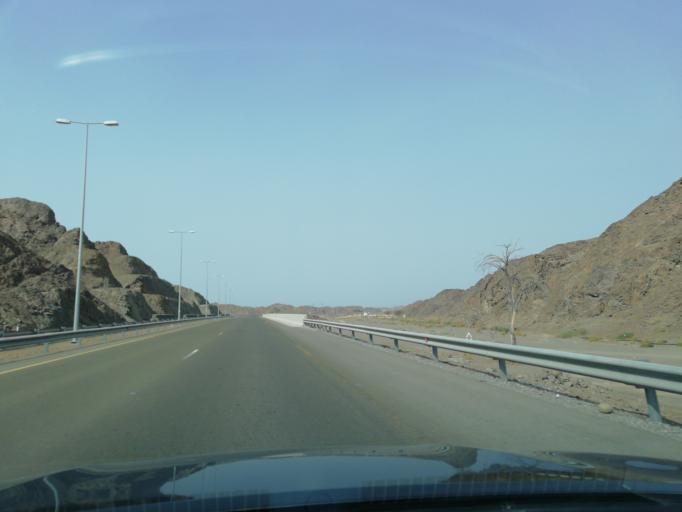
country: OM
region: Al Batinah
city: Al Liwa'
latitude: 24.3379
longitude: 56.4972
